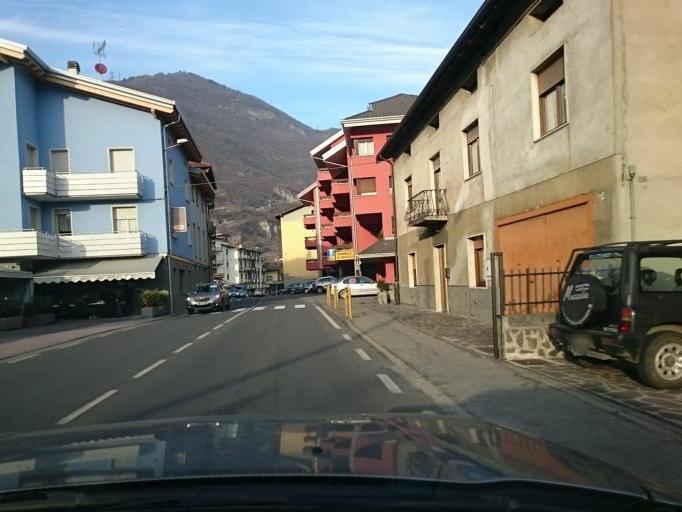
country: IT
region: Lombardy
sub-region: Provincia di Brescia
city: Malegno
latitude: 45.9479
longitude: 10.2769
